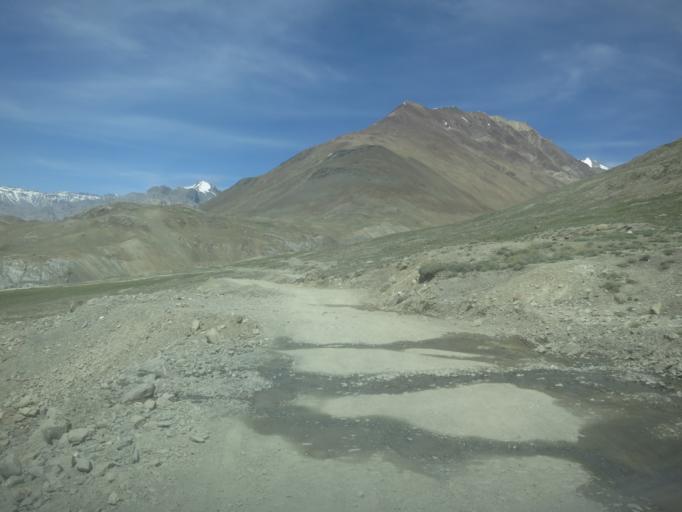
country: IN
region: Himachal Pradesh
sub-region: Kulu
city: Manali
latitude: 32.4013
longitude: 77.6394
